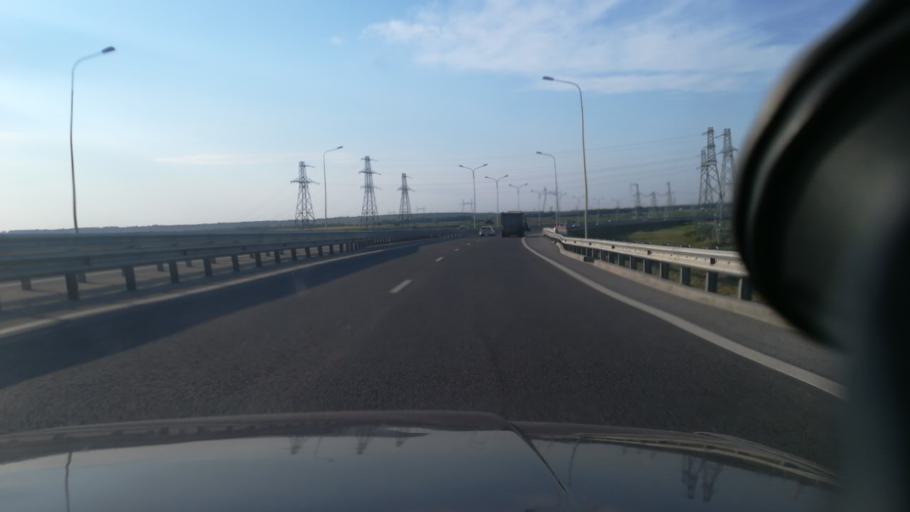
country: RU
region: Krasnodarskiy
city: Dzhiginka
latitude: 45.1252
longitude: 37.3112
